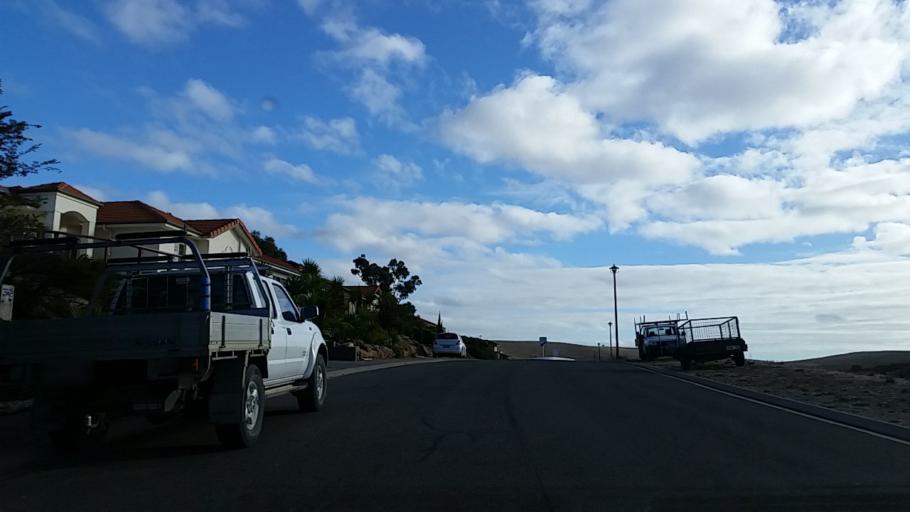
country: AU
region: South Australia
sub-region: Yankalilla
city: Normanville
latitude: -35.5025
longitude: 138.2496
